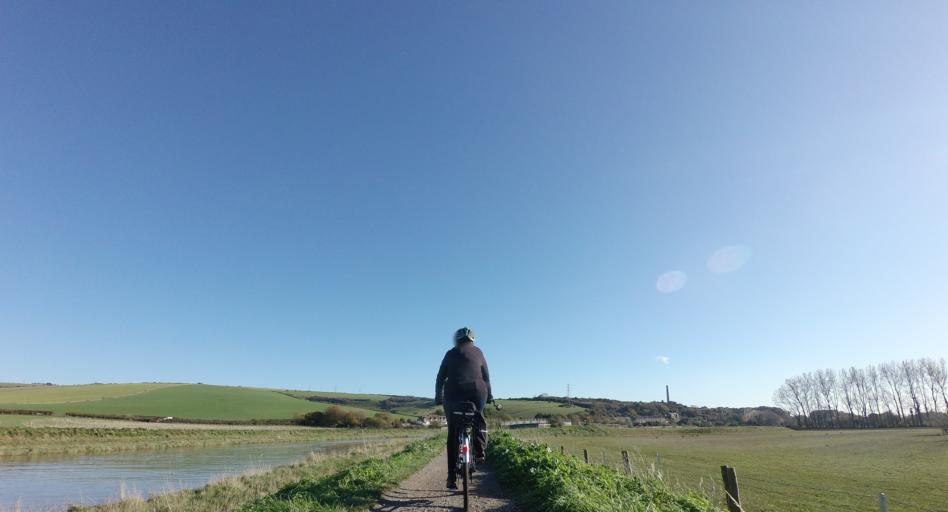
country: GB
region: England
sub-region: West Sussex
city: Steyning
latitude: 50.8716
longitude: -0.3027
